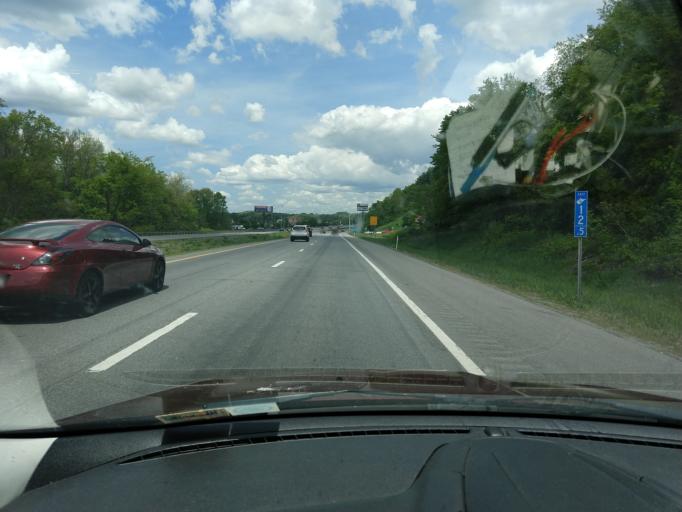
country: US
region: West Virginia
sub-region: Mercer County
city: Princeton
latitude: 37.3558
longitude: -81.0988
